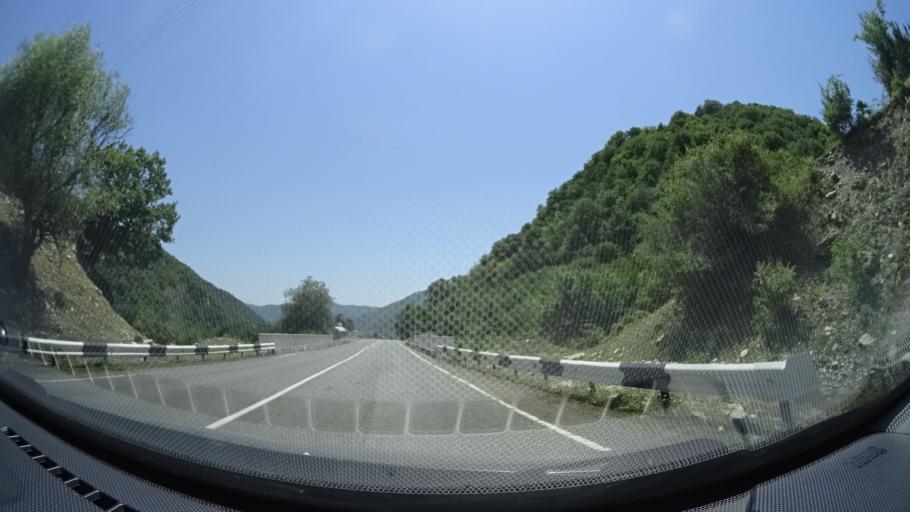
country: GE
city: Zhinvali
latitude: 42.2004
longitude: 44.6751
